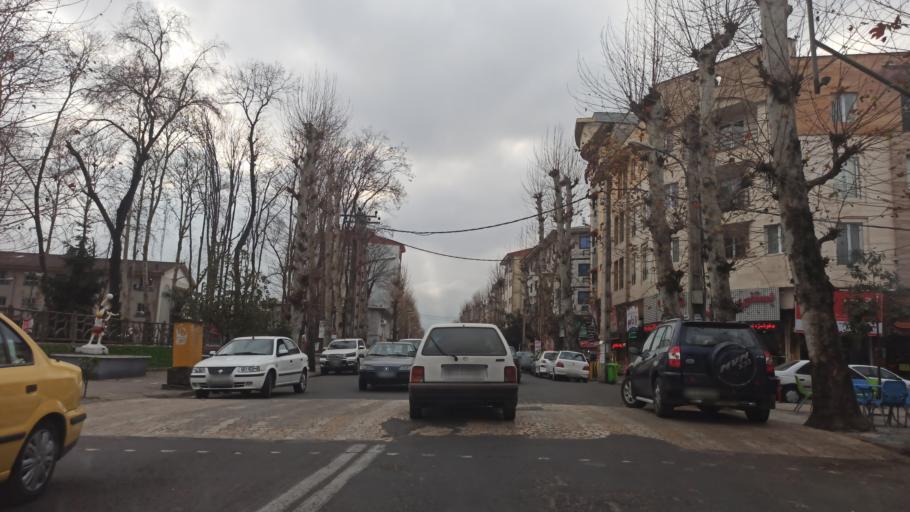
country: IR
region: Gilan
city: Fuman
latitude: 37.2314
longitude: 49.3178
